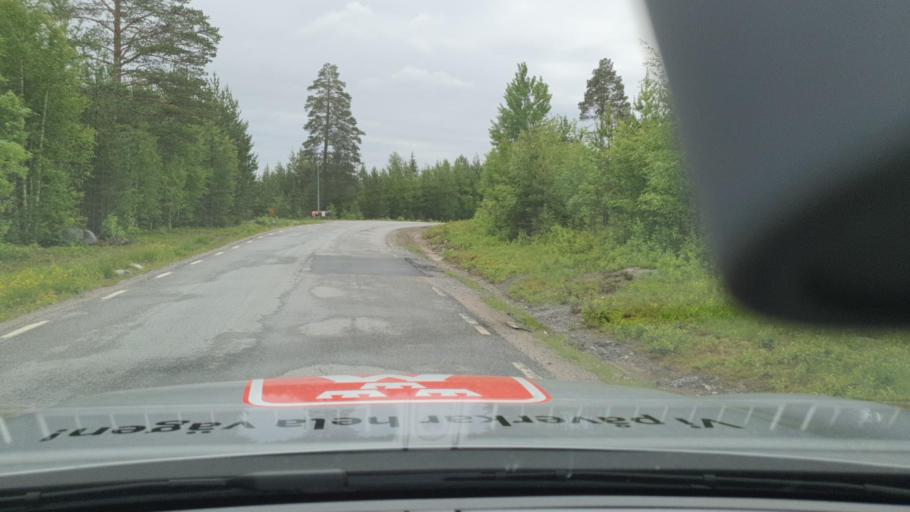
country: SE
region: Norrbotten
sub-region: Lulea Kommun
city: Ranea
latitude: 65.7849
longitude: 22.2965
